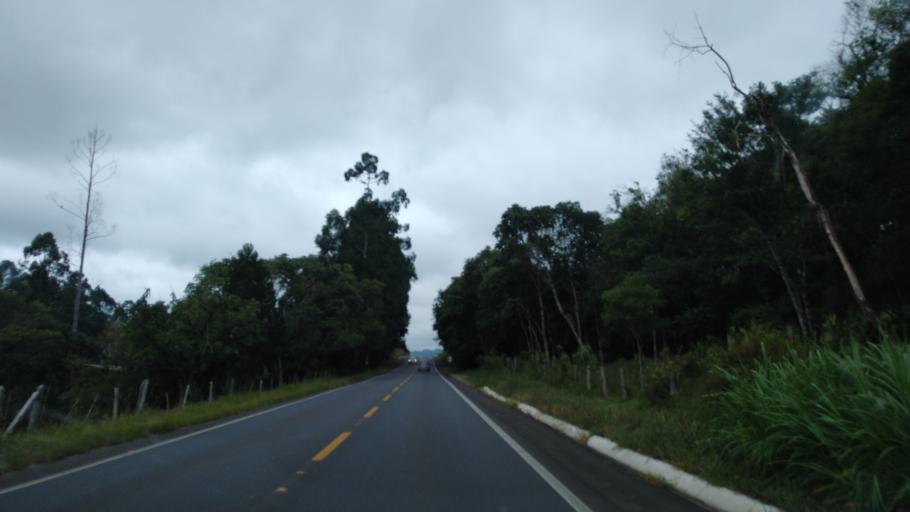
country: BR
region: Santa Catarina
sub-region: Porto Uniao
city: Porto Uniao
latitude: -26.2816
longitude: -51.0016
